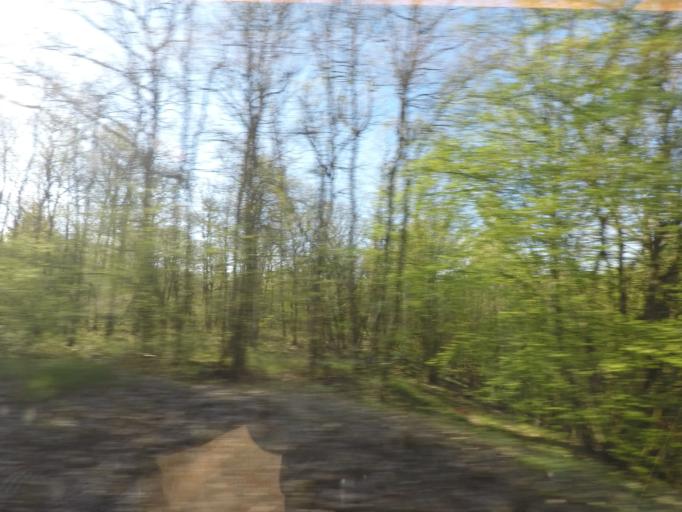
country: BE
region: Wallonia
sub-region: Province du Luxembourg
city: Marche-en-Famenne
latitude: 50.2489
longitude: 5.2560
